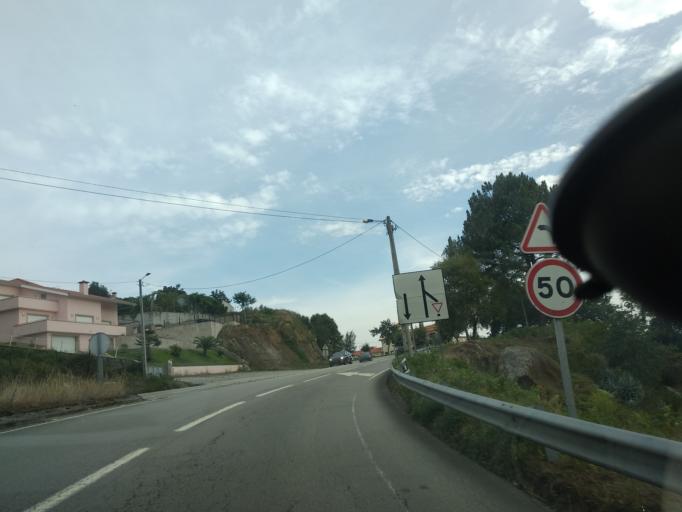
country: PT
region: Braga
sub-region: Povoa de Lanhoso
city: Povoa de Lanhoso
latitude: 41.6128
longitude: -8.2499
